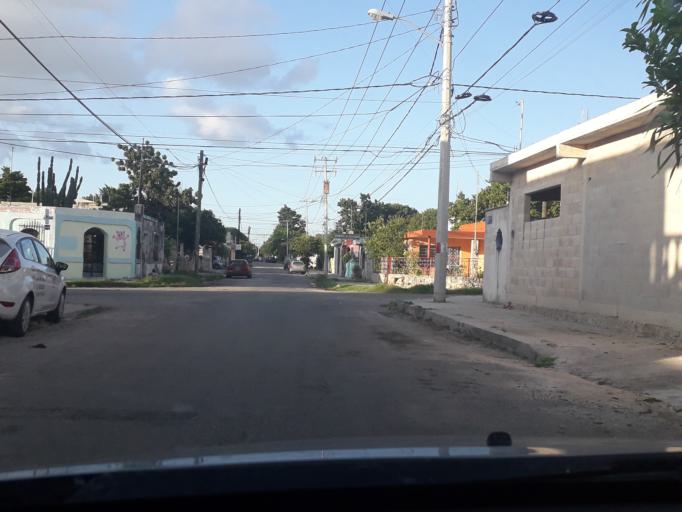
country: MX
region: Yucatan
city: Merida
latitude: 20.9736
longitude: -89.6466
